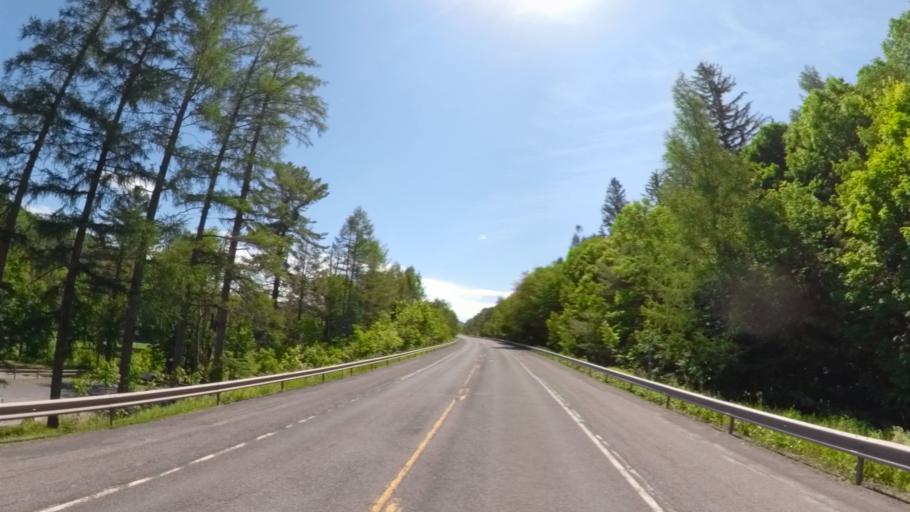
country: US
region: New York
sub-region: Delaware County
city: Stamford
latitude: 42.1540
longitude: -74.5411
